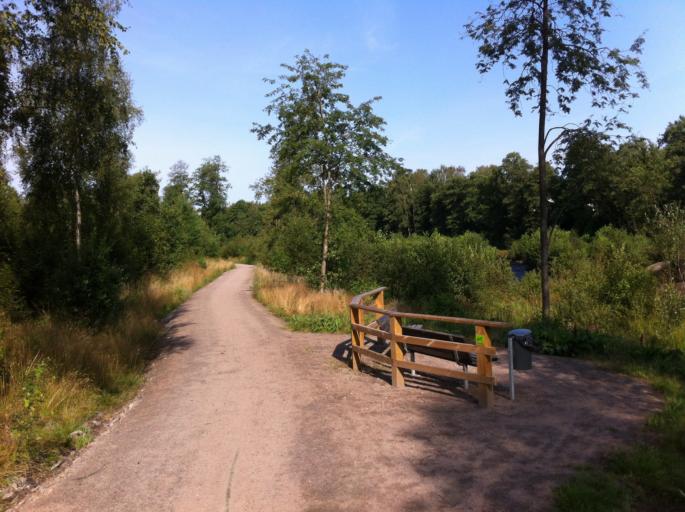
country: SE
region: Halland
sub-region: Hylte Kommun
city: Hyltebruk
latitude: 57.0039
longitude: 13.2445
